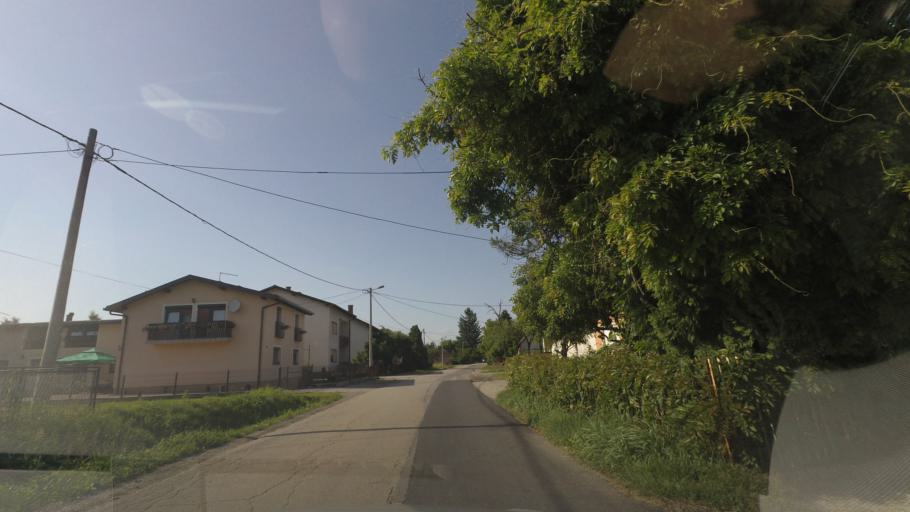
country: HR
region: Karlovacka
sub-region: Grad Karlovac
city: Karlovac
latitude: 45.5064
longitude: 15.5312
